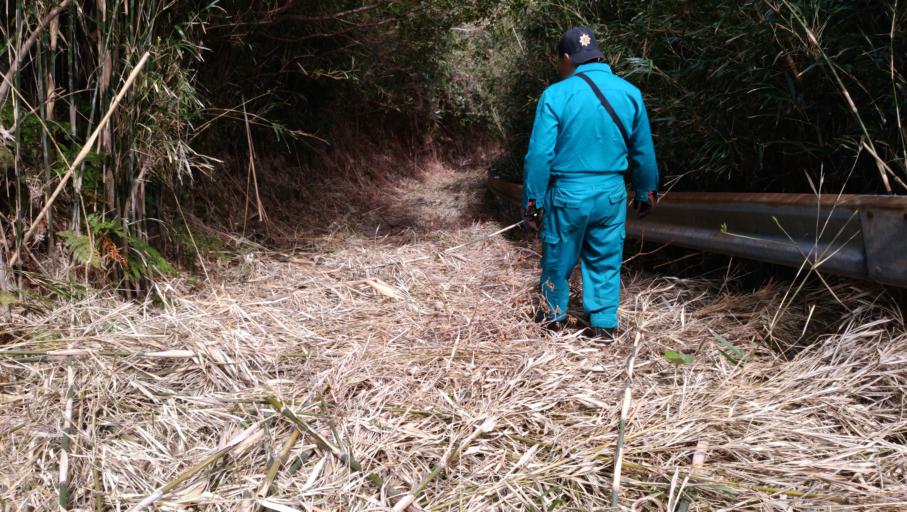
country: JP
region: Kagoshima
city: Makurazaki
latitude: 30.7856
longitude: 130.2766
